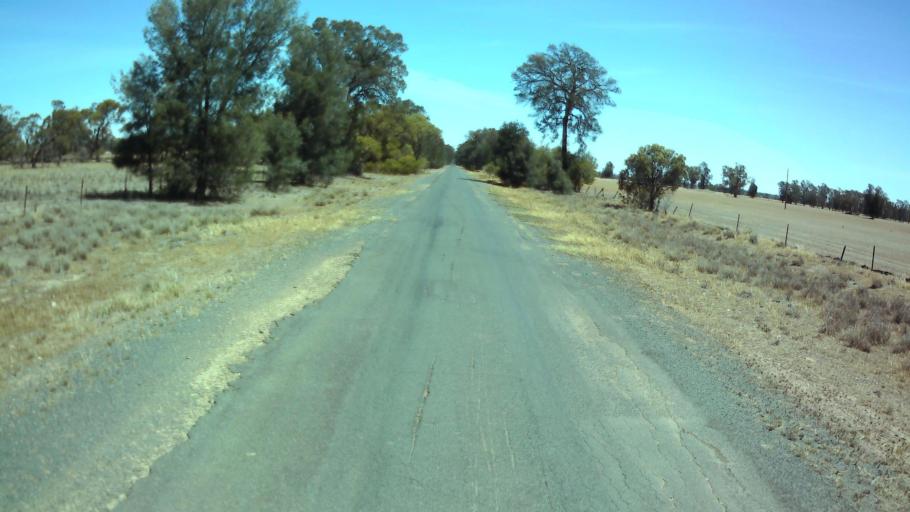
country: AU
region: New South Wales
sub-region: Weddin
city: Grenfell
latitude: -33.8744
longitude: 147.6913
